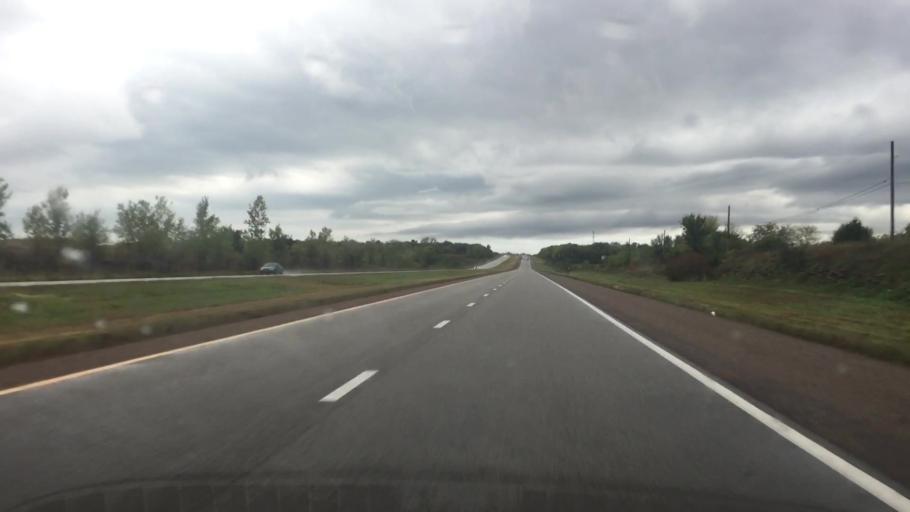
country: US
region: Kansas
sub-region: Miami County
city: Paola
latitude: 38.6047
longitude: -94.8356
